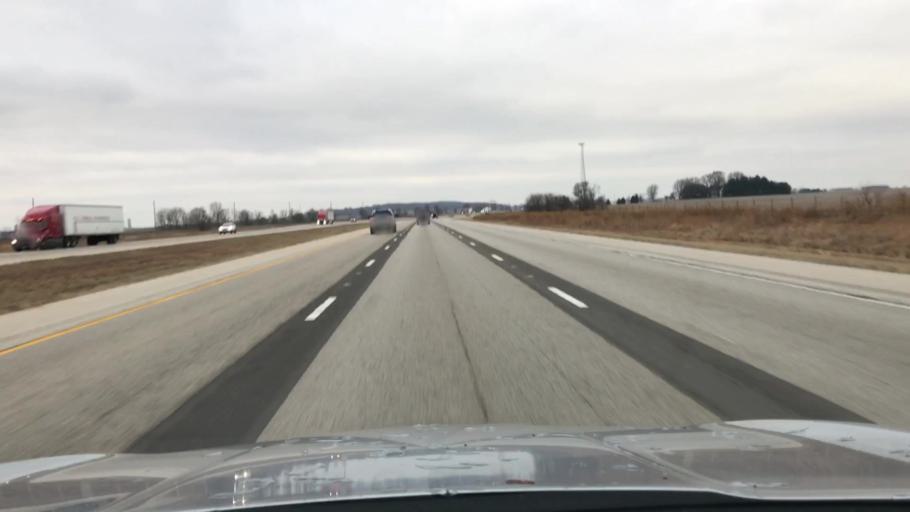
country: US
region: Illinois
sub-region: Logan County
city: Lincoln
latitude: 40.0633
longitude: -89.4493
